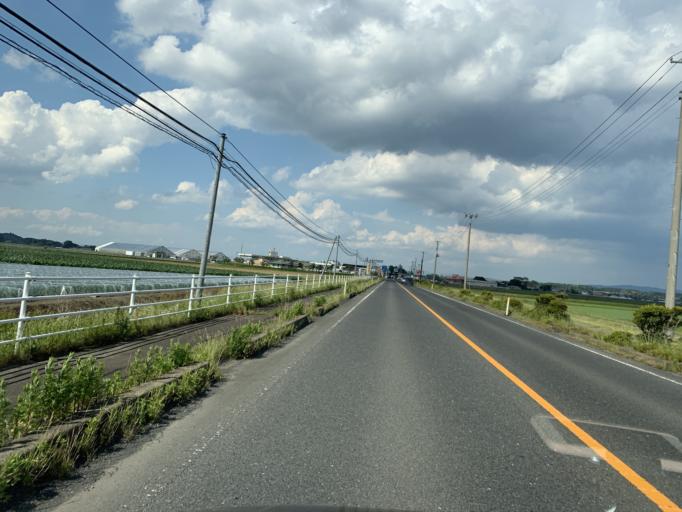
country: JP
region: Miyagi
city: Wakuya
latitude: 38.6242
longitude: 141.1863
